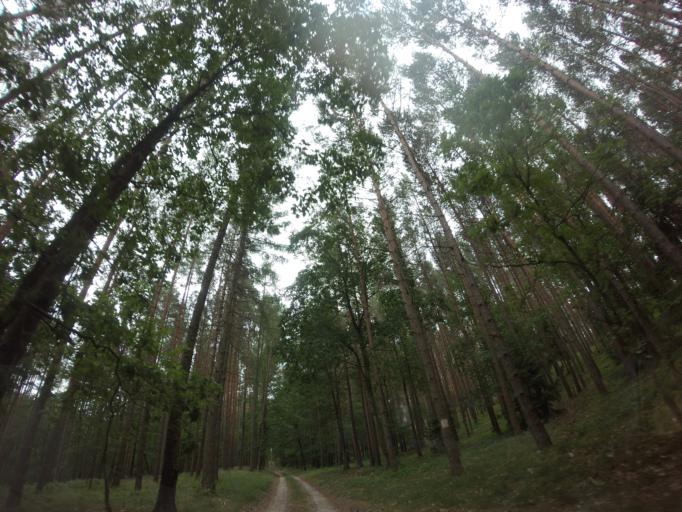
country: PL
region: West Pomeranian Voivodeship
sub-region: Powiat choszczenski
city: Bierzwnik
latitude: 52.9719
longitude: 15.6132
